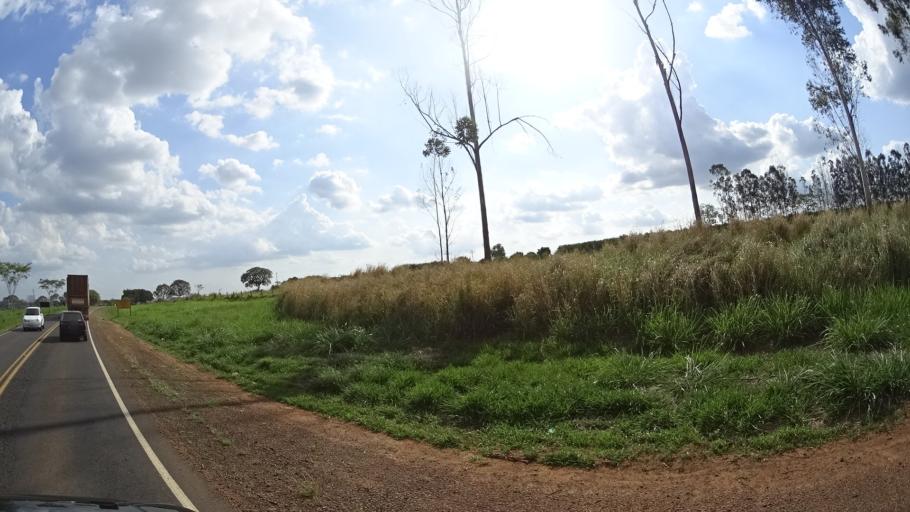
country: BR
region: Sao Paulo
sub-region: Urupes
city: Urupes
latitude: -21.1807
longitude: -49.2928
